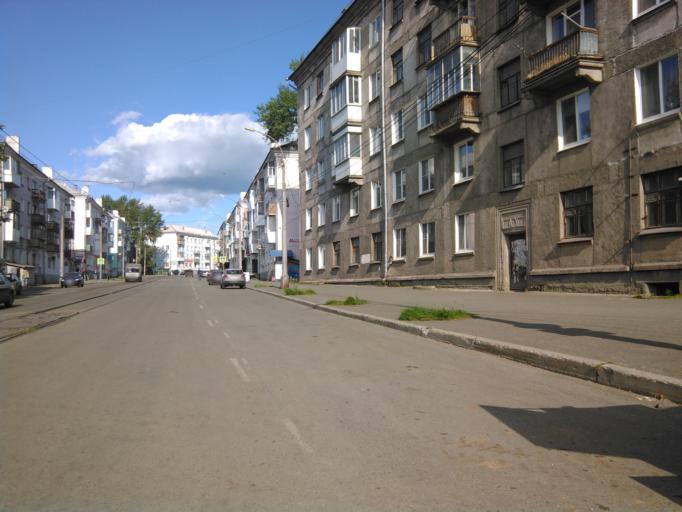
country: RU
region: Sverdlovsk
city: Krasnotur'insk
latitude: 59.7672
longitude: 60.1893
